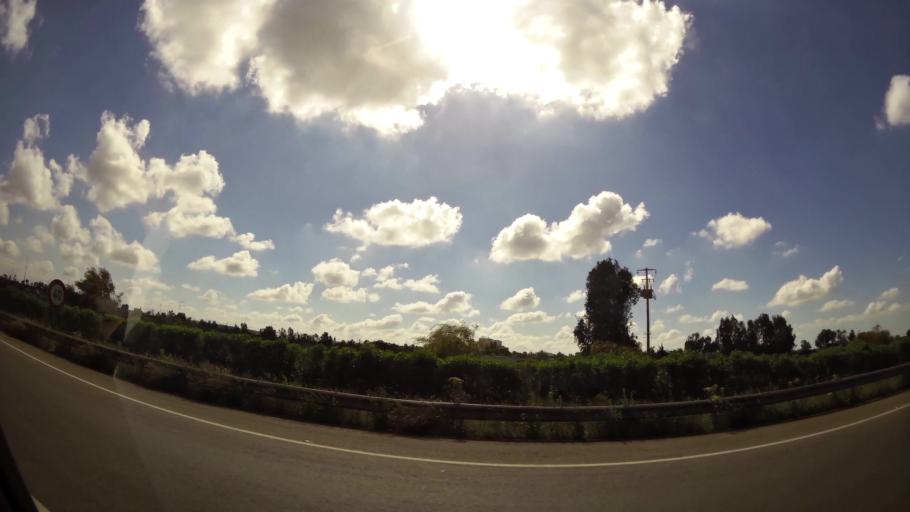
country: MA
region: Grand Casablanca
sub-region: Nouaceur
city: Bouskoura
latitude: 33.4401
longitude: -7.6303
